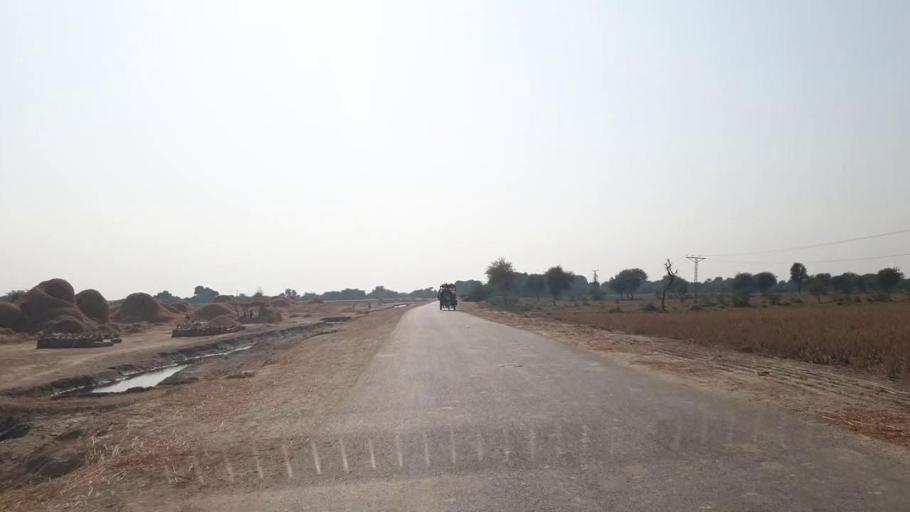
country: PK
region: Sindh
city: Matli
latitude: 24.9737
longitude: 68.6514
